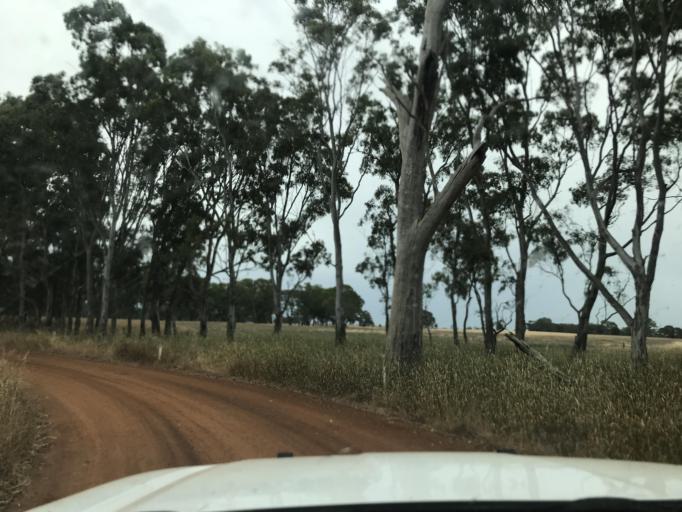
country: AU
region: Victoria
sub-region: Horsham
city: Horsham
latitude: -37.0650
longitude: 141.6755
